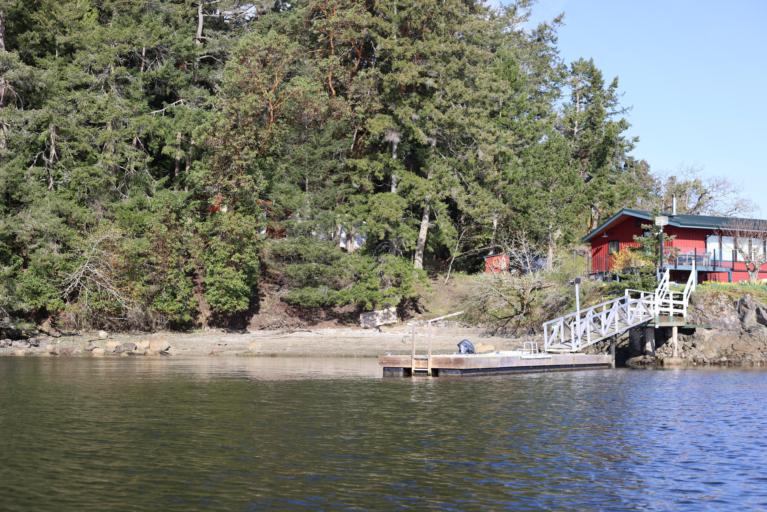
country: CA
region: British Columbia
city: North Saanich
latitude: 48.5726
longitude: -123.4733
